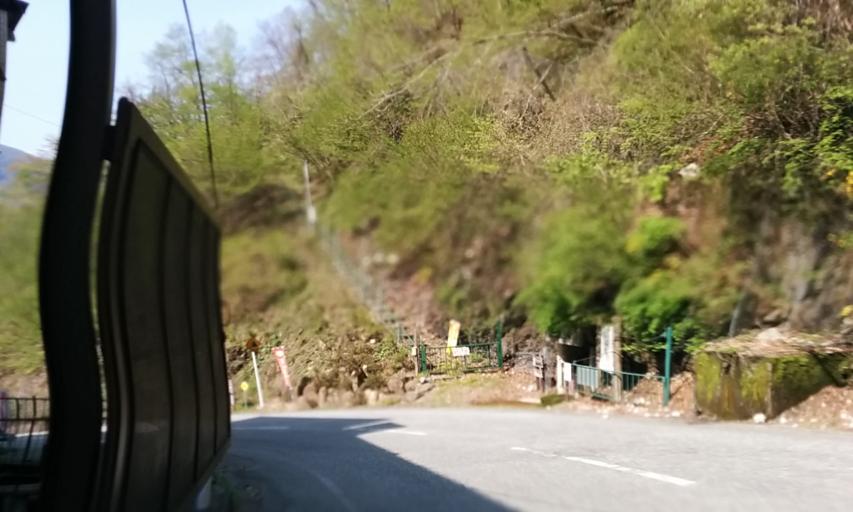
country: JP
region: Gifu
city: Takayama
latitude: 36.1843
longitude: 137.4242
